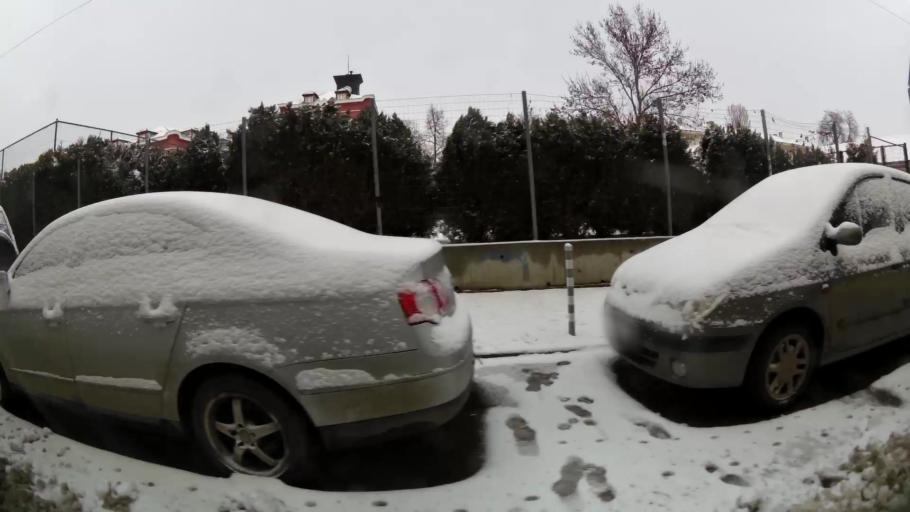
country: BG
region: Sofia-Capital
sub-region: Stolichna Obshtina
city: Sofia
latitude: 42.7046
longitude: 23.3131
